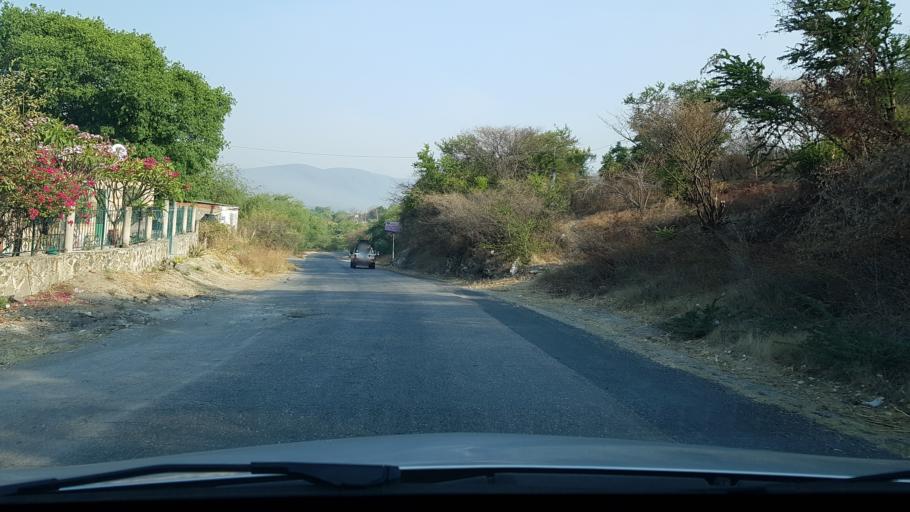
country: MX
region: Morelos
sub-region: Tlaltizapan de Zapata
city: Colonia Palo Prieto (Chipitongo)
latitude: 18.6938
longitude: -99.1006
